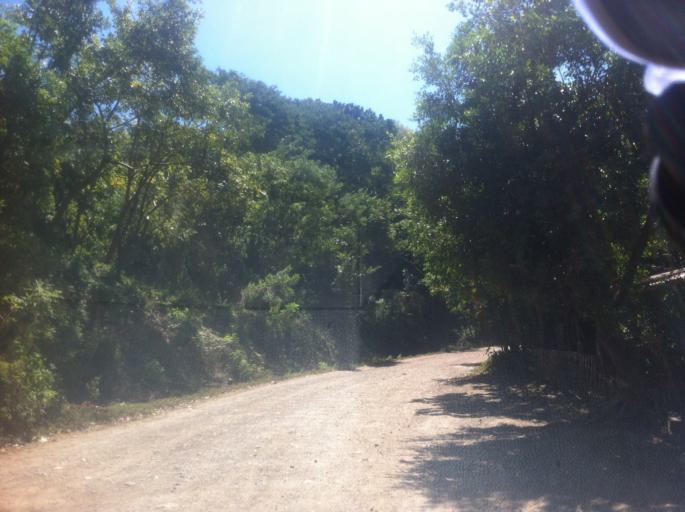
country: NI
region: Matagalpa
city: San Dionisio
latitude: 12.8227
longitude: -85.8483
